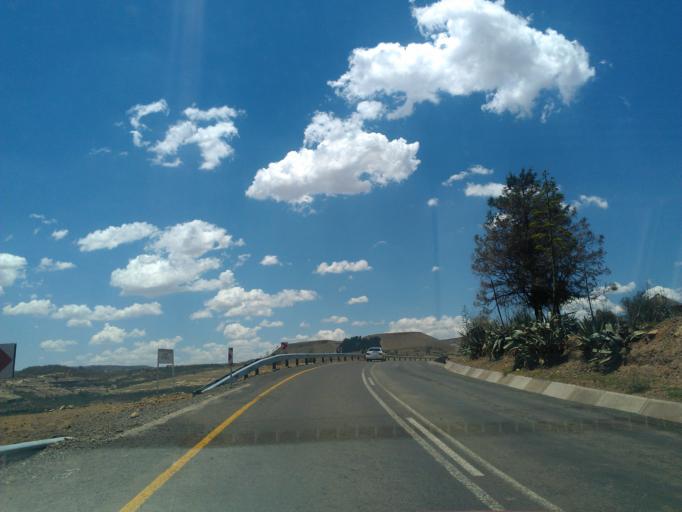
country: LS
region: Leribe
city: Maputsoe
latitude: -29.0916
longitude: 27.9592
